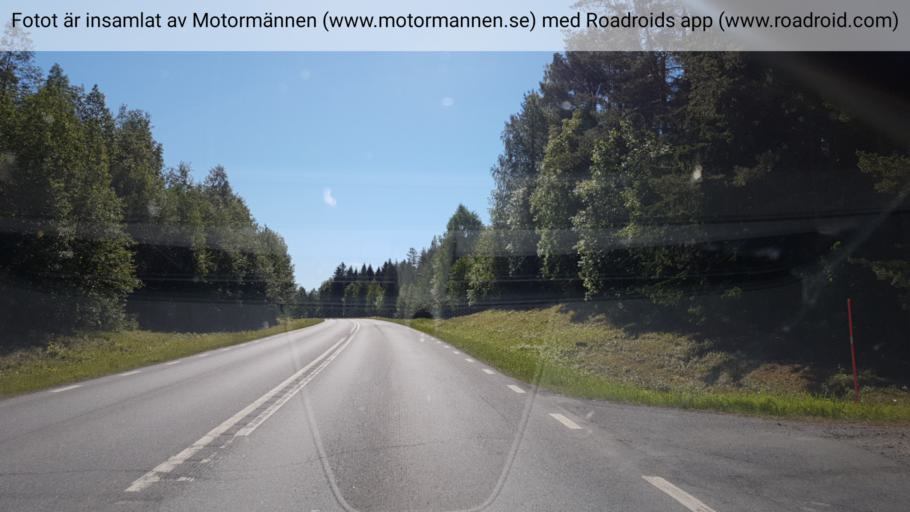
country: SE
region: Norrbotten
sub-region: Bodens Kommun
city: Boden
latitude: 65.8626
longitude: 21.4244
